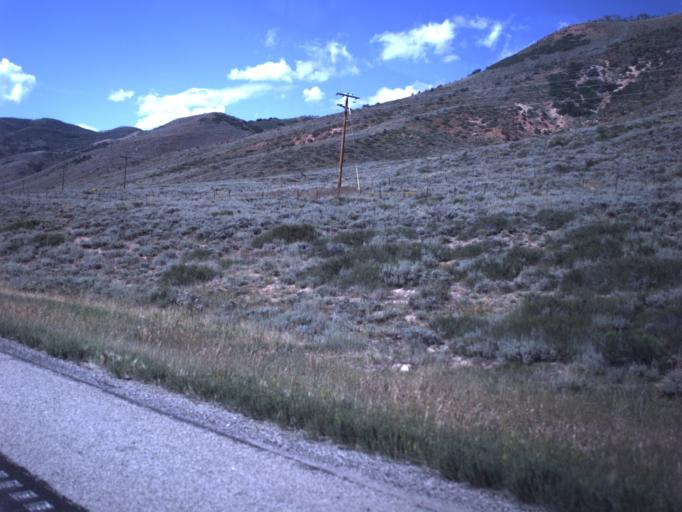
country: US
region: Utah
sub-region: Wasatch County
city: Heber
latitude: 40.2222
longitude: -111.1054
